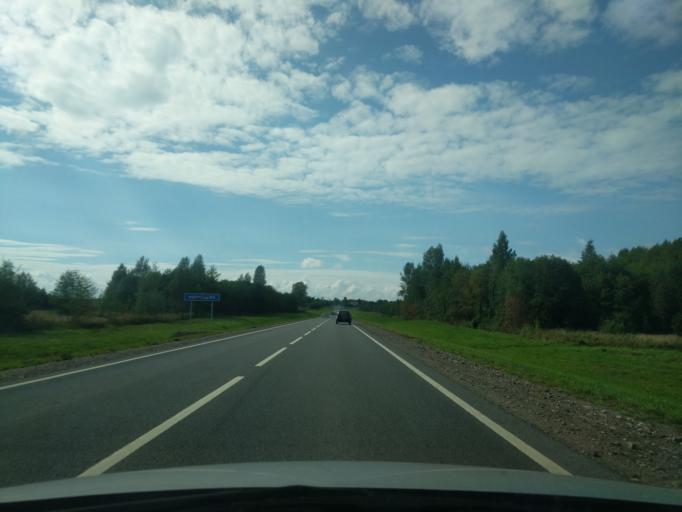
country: RU
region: Kostroma
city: Oktyabr'skiy
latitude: 57.7979
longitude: 41.2230
